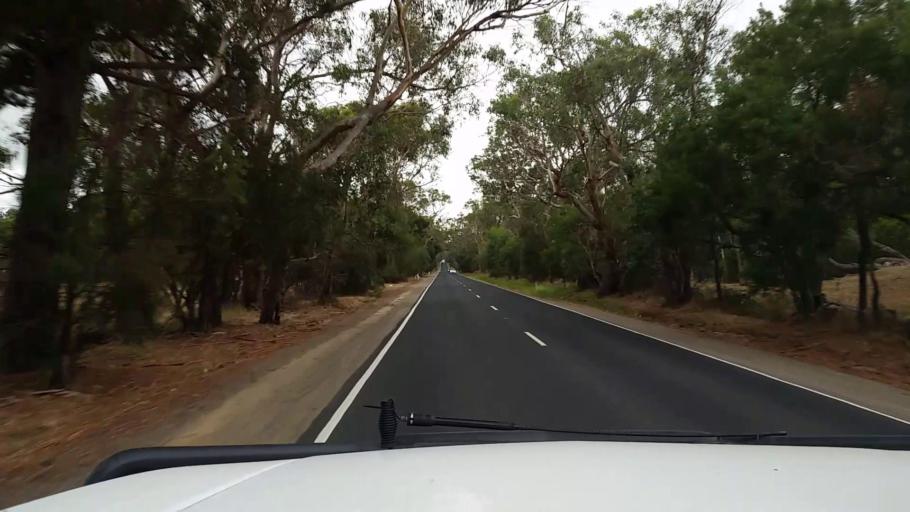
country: AU
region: Victoria
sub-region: Mornington Peninsula
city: Somerville
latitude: -38.2322
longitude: 145.1520
